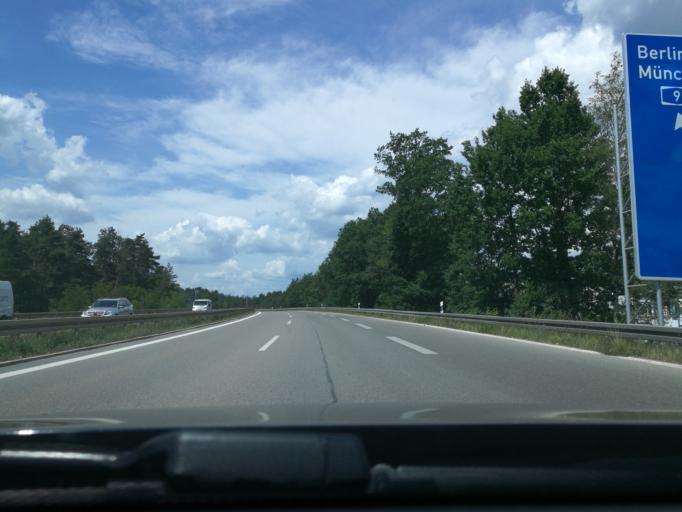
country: DE
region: Bavaria
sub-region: Regierungsbezirk Mittelfranken
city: Feucht
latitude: 49.3662
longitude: 11.2049
